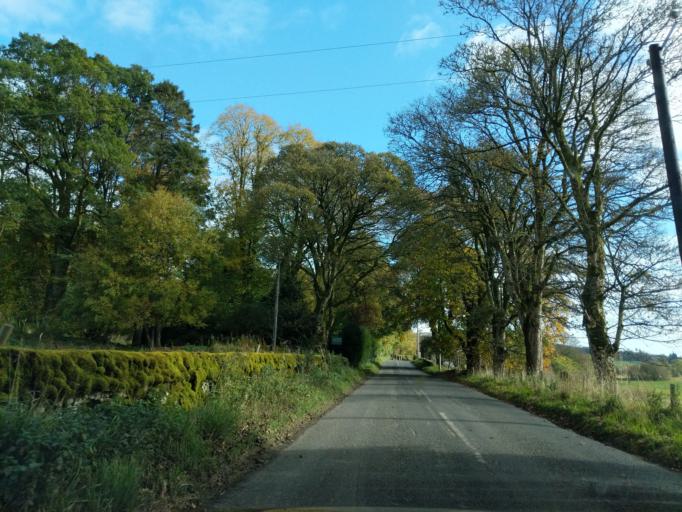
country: GB
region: Scotland
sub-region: Dumfries and Galloway
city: Thornhill
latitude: 55.1941
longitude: -3.8783
